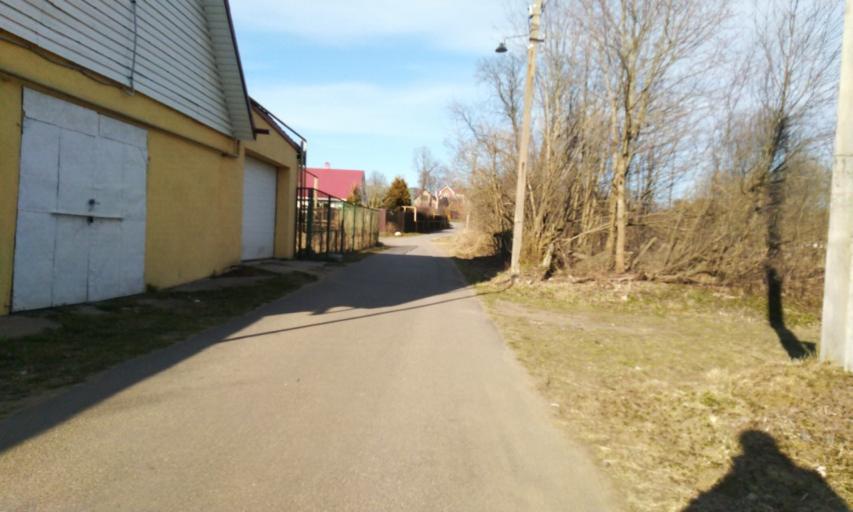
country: RU
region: Leningrad
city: Toksovo
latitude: 60.1216
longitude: 30.5007
